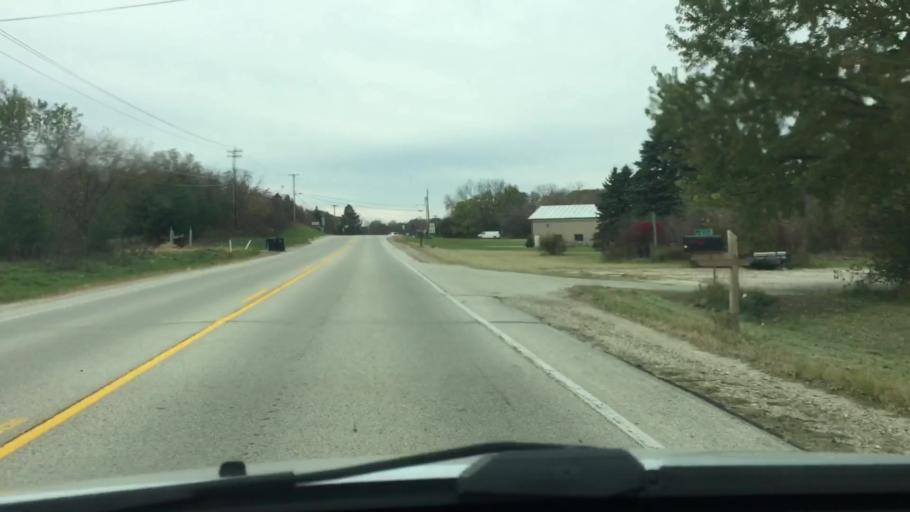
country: US
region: Wisconsin
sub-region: Waukesha County
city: Mukwonago
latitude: 42.8942
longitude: -88.2753
